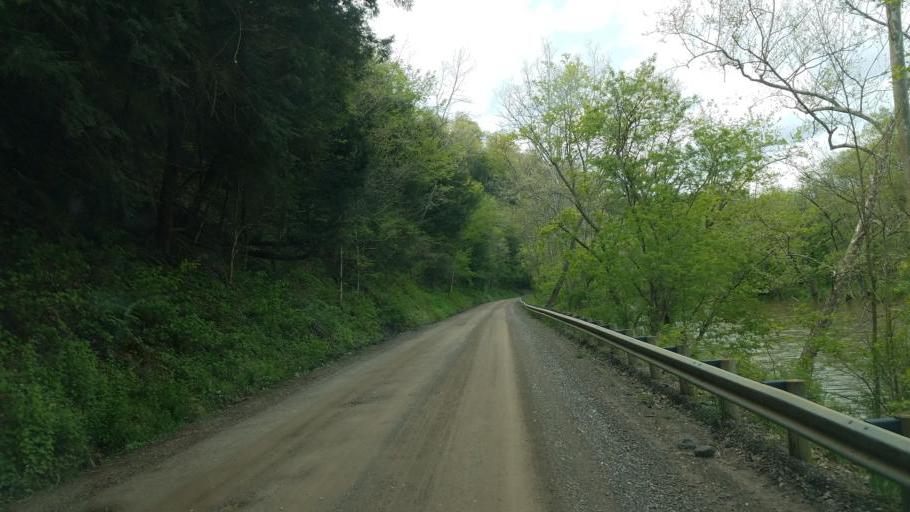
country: US
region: Ohio
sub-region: Ashland County
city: Loudonville
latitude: 40.5387
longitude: -82.2069
